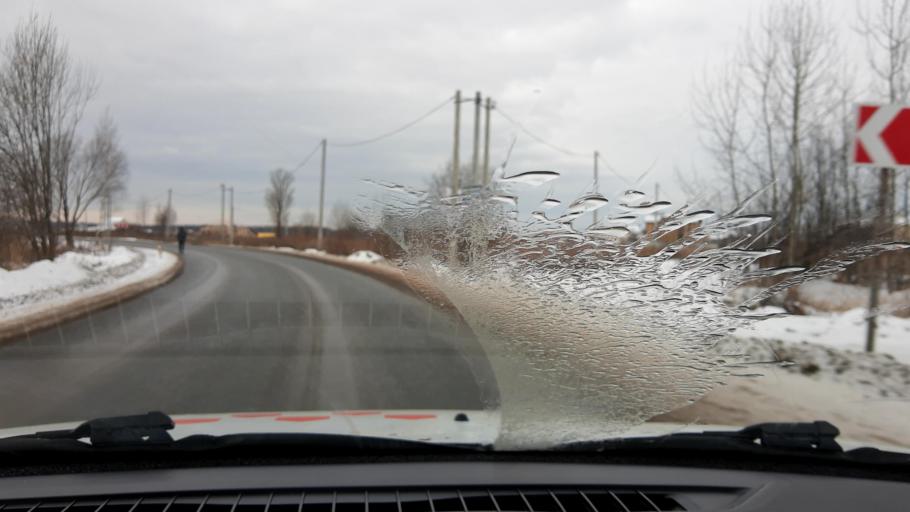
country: RU
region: Nizjnij Novgorod
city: Neklyudovo
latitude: 56.4237
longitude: 43.9581
